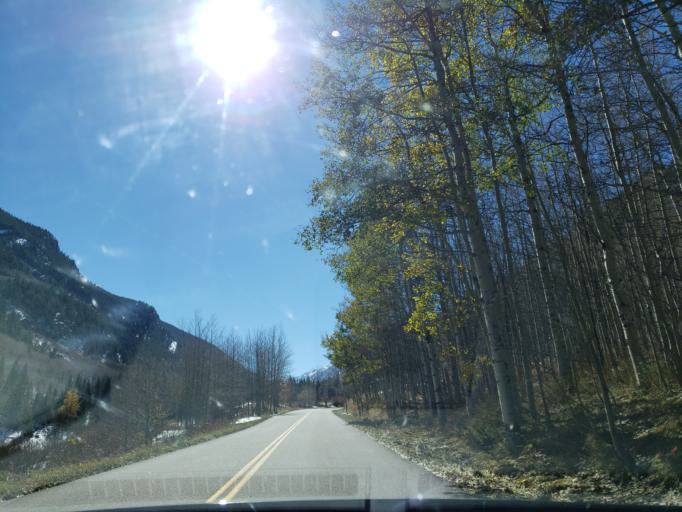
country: US
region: Colorado
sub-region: Pitkin County
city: Snowmass Village
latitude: 39.1376
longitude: -106.8991
